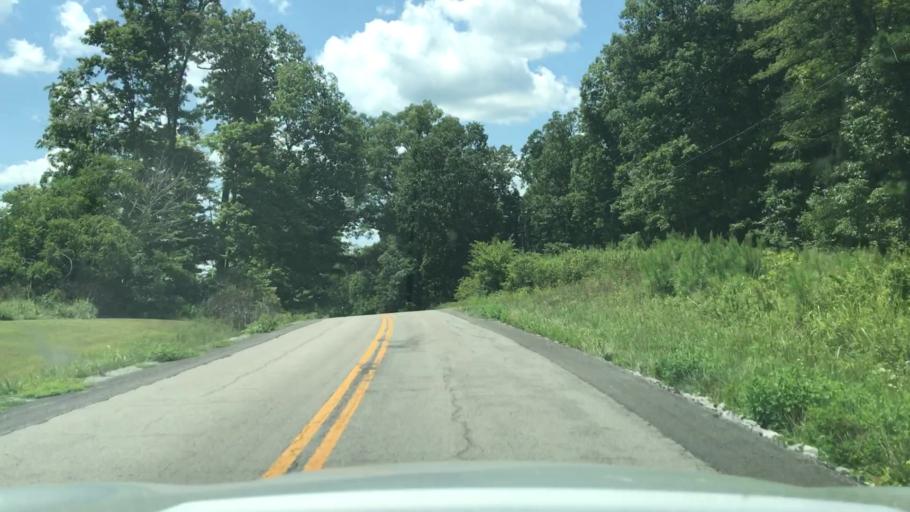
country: US
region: Kentucky
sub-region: Hopkins County
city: Nortonville
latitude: 37.1244
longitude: -87.3143
